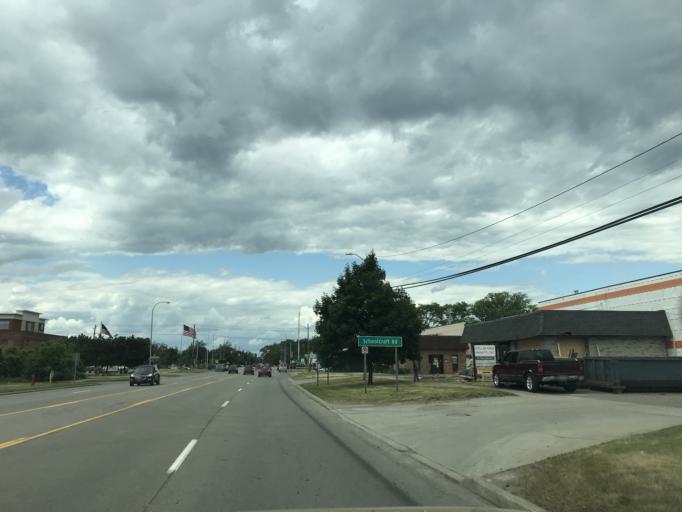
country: US
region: Michigan
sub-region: Wayne County
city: Redford
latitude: 42.3818
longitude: -83.3140
